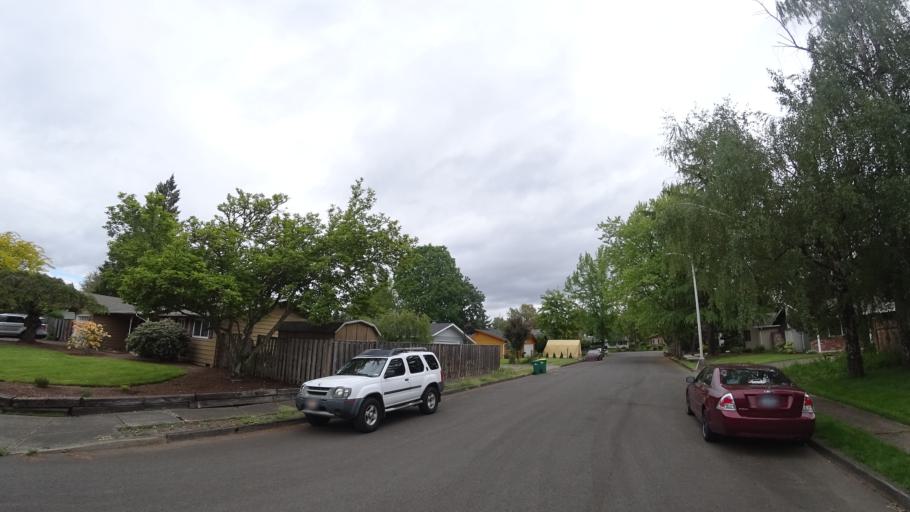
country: US
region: Oregon
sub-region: Washington County
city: Beaverton
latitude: 45.4747
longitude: -122.8092
